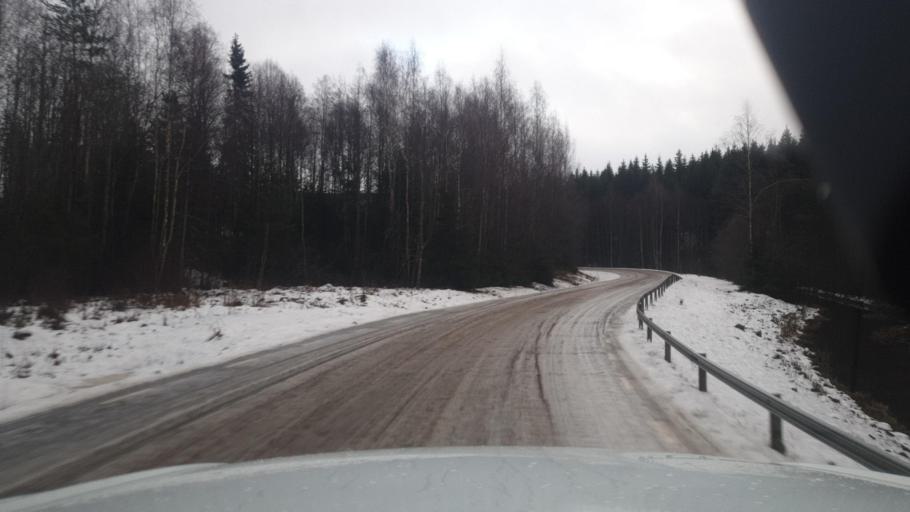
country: SE
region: Vaermland
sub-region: Torsby Kommun
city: Torsby
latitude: 59.9796
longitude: 12.8085
